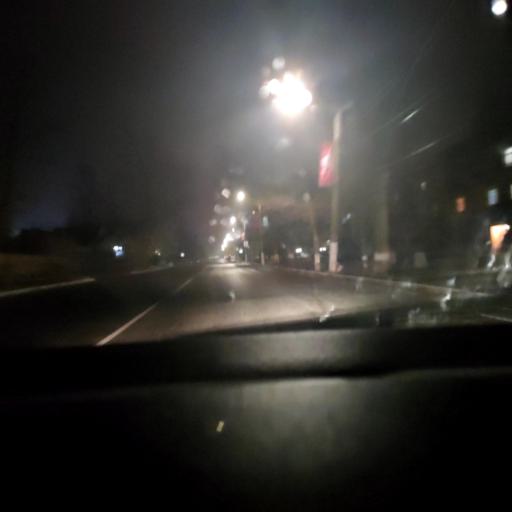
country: RU
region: Voronezj
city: Semiluki
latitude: 51.6847
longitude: 39.0339
